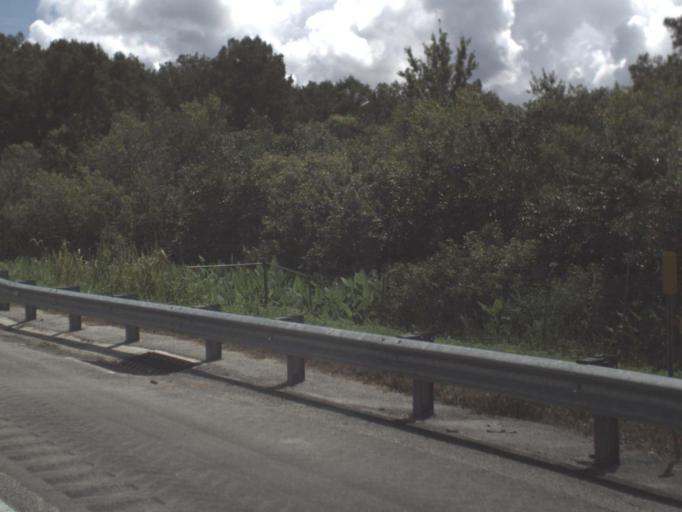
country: US
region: Florida
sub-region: Collier County
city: Orangetree
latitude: 26.1539
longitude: -81.3899
